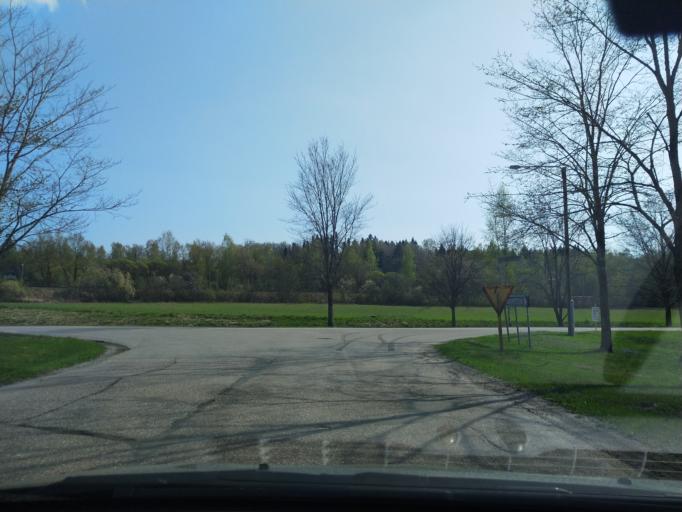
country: FI
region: Uusimaa
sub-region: Helsinki
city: Lohja
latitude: 60.1841
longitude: 23.9831
